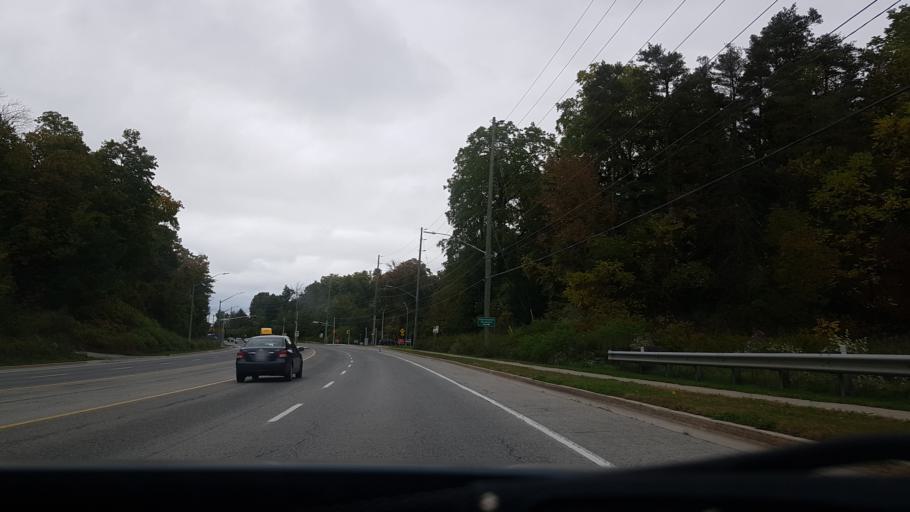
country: CA
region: Ontario
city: Newmarket
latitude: 44.0340
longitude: -79.4967
